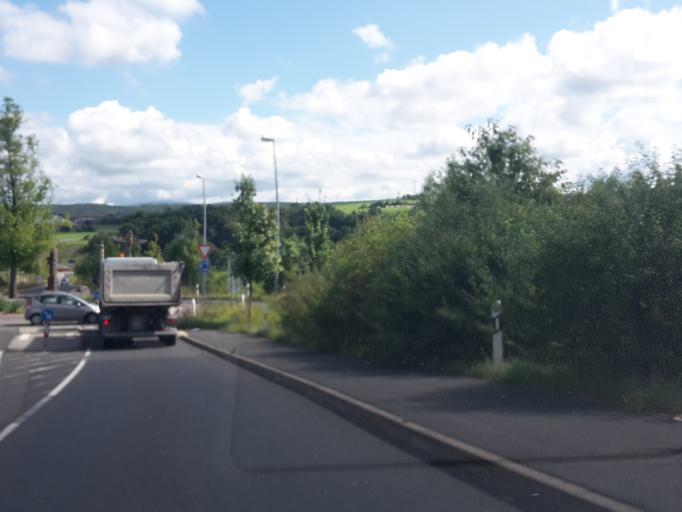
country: DE
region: Hesse
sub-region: Regierungsbezirk Darmstadt
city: Idstein
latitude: 50.2073
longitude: 8.2623
